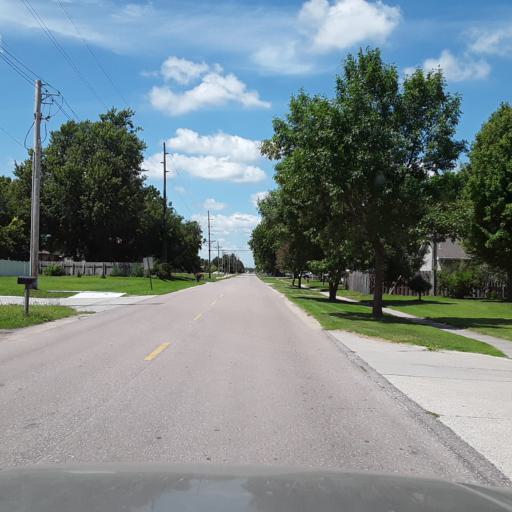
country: US
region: Nebraska
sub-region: Merrick County
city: Central City
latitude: 41.1048
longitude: -98.0081
